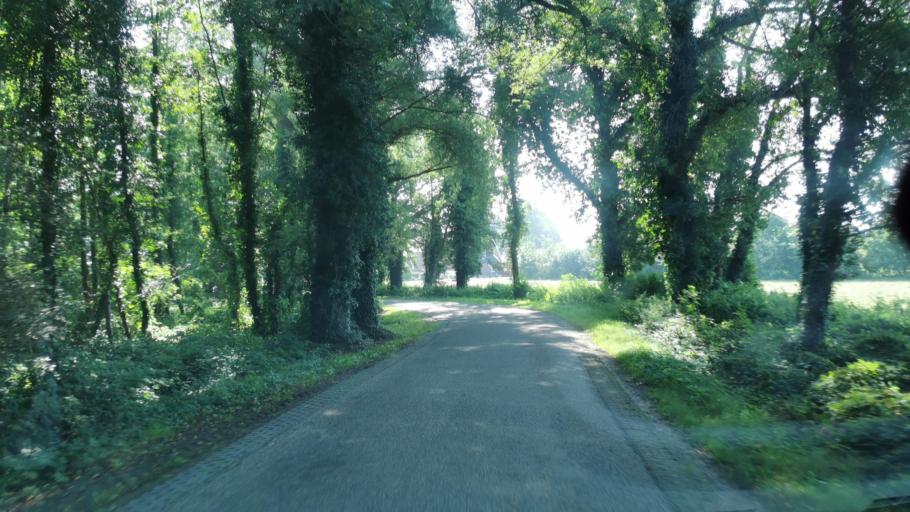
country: NL
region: Overijssel
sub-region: Gemeente Tubbergen
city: Tubbergen
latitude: 52.3473
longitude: 6.8153
